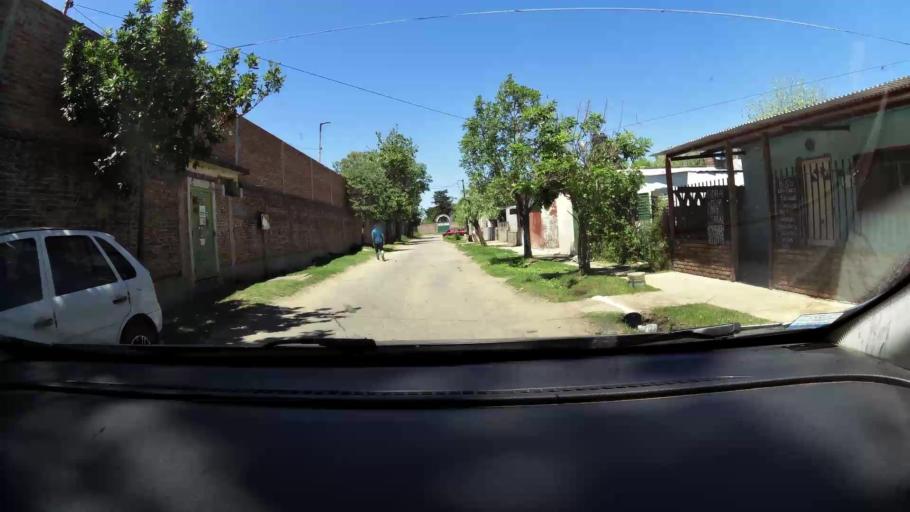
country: AR
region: Santa Fe
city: Santa Fe de la Vera Cruz
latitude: -31.6134
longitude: -60.7195
